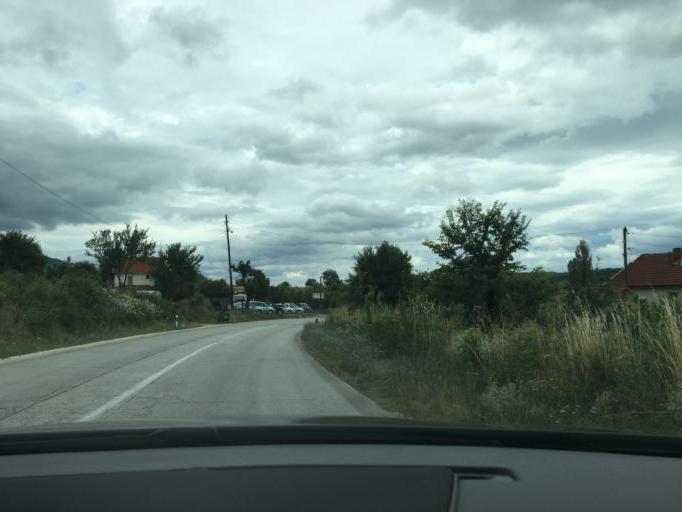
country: MK
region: Kriva Palanka
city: Kriva Palanka
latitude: 42.1786
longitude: 22.2661
